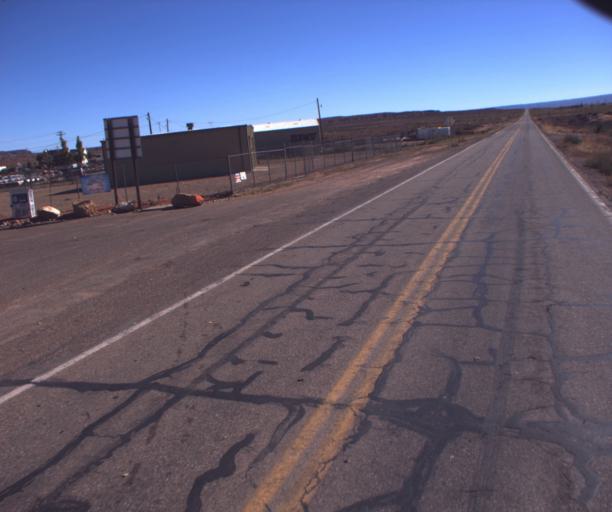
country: US
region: Arizona
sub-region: Coconino County
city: Fredonia
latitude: 36.9396
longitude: -112.5215
